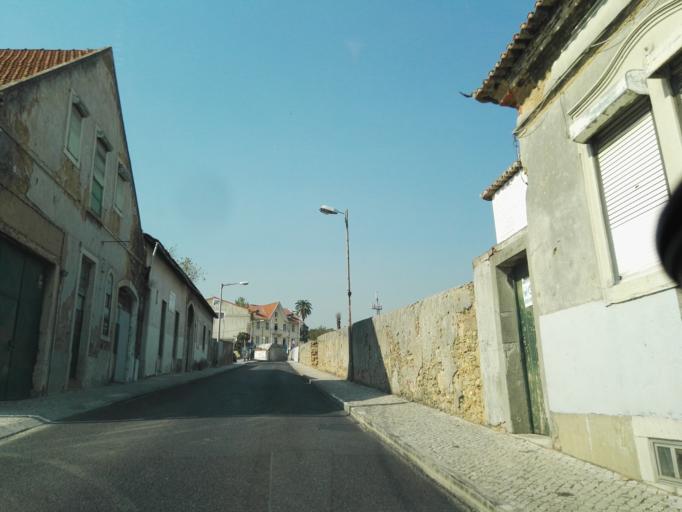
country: PT
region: Lisbon
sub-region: Lisbon
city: Lisbon
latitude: 38.7304
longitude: -9.1090
